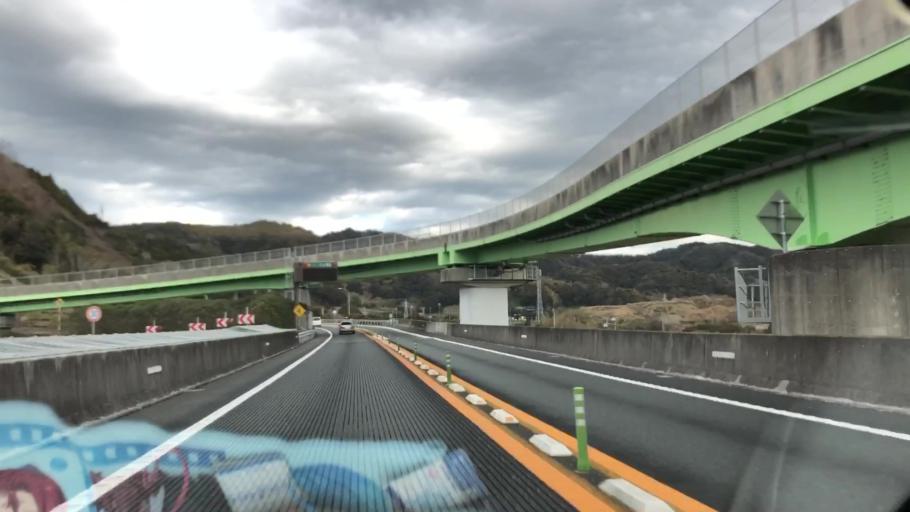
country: JP
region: Chiba
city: Tateyama
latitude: 35.1139
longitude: 139.8512
